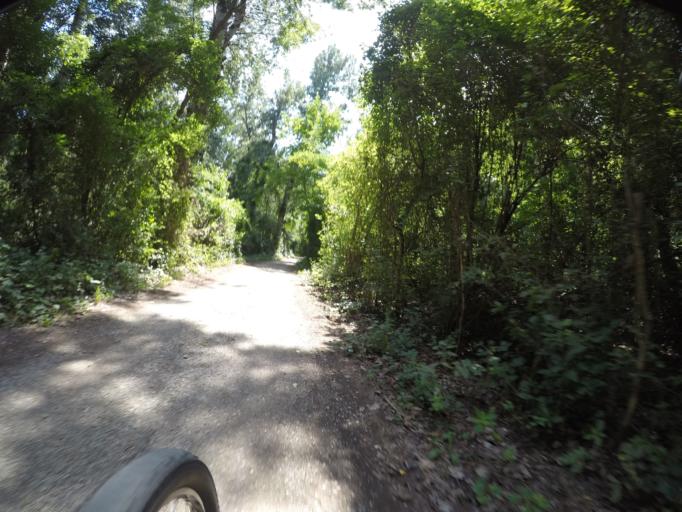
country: AT
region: Lower Austria
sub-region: Politischer Bezirk Ganserndorf
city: Gross-Enzersdorf
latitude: 48.1855
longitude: 16.5356
